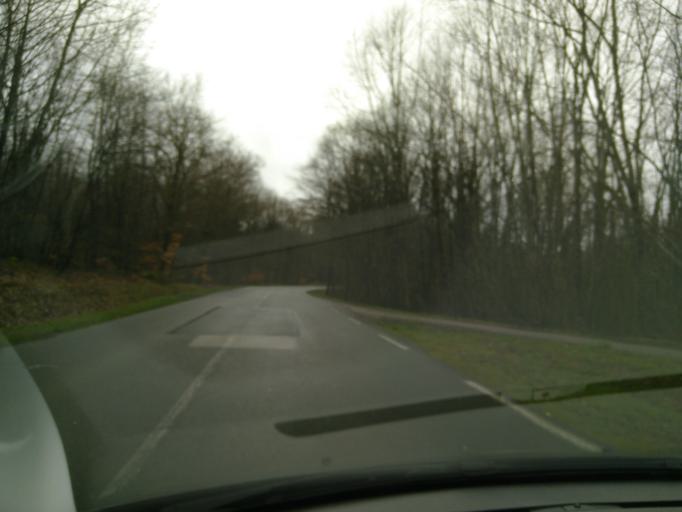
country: FR
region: Limousin
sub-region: Departement de la Haute-Vienne
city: Solignac
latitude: 45.7270
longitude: 1.2581
